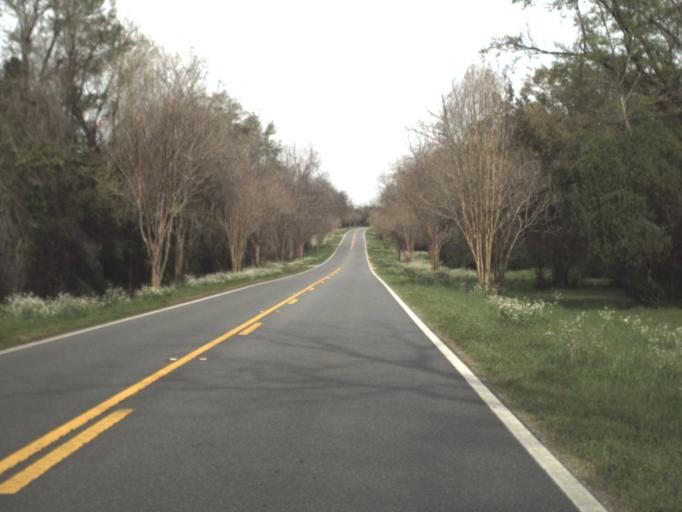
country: US
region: Florida
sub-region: Jefferson County
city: Monticello
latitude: 30.5208
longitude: -84.0346
